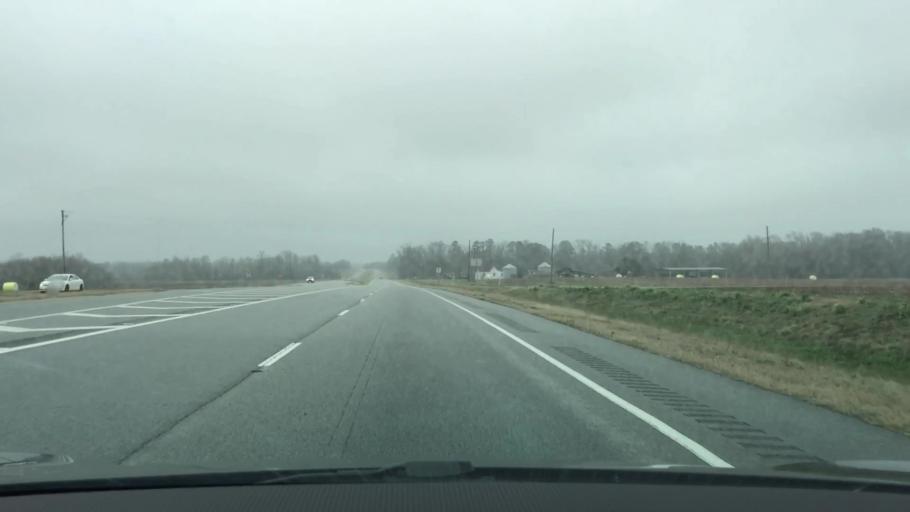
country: US
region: Georgia
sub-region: Jefferson County
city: Wadley
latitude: 32.8292
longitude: -82.4021
